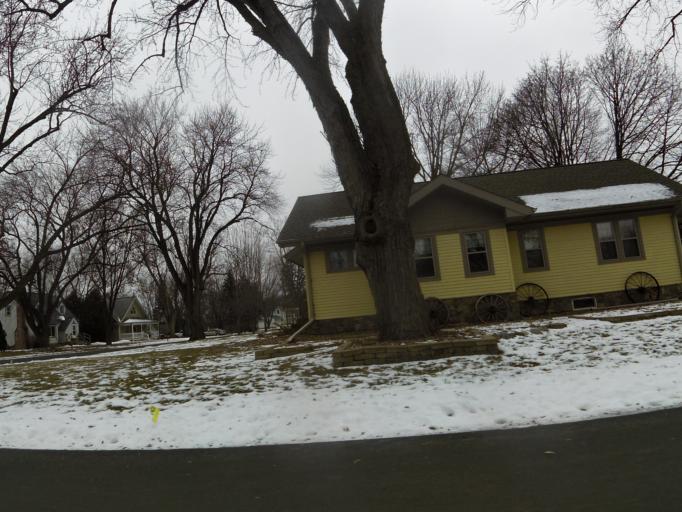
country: US
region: Minnesota
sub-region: Carver County
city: Watertown
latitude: 44.9607
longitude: -93.8519
